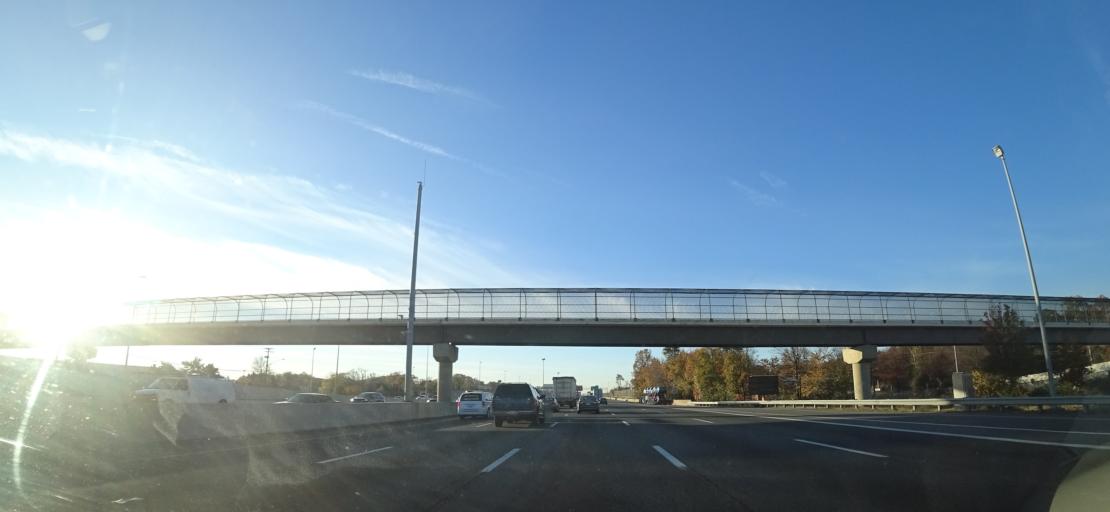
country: US
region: Virginia
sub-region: Fairfax County
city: Springfield
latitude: 38.7683
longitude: -77.1831
